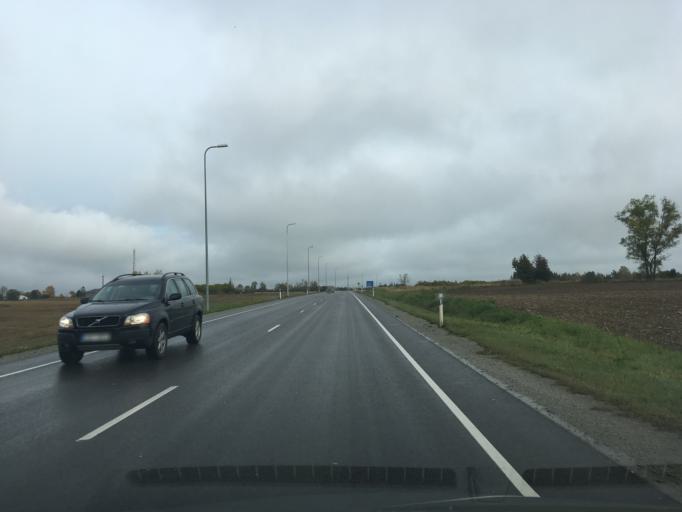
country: EE
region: Harju
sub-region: Saue linn
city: Saue
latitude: 59.3560
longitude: 24.4932
